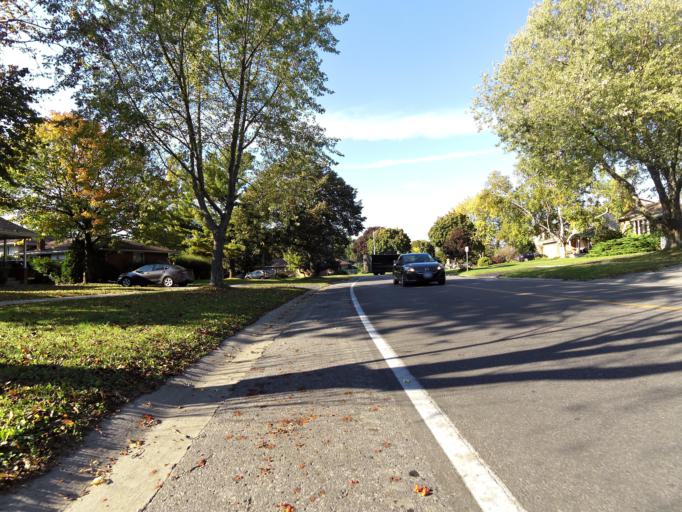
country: CA
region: Ontario
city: Kingston
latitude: 44.2305
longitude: -76.5326
